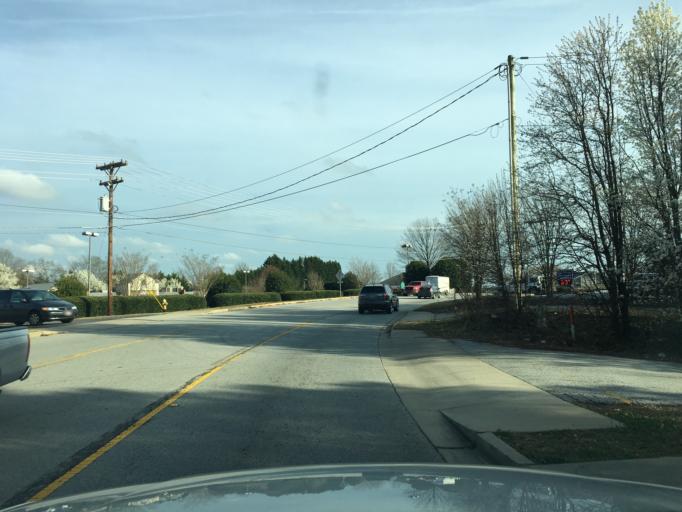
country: US
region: South Carolina
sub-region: Greenville County
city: Taylors
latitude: 34.8941
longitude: -82.2905
